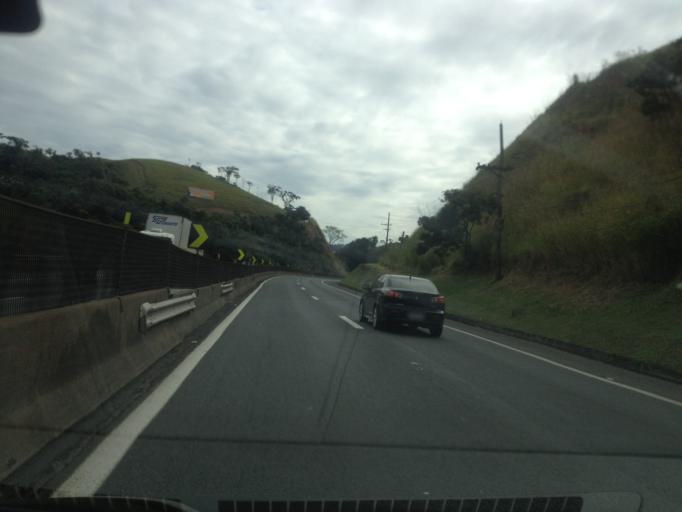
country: BR
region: Rio de Janeiro
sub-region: Pirai
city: Pirai
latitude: -22.6423
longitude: -43.8977
